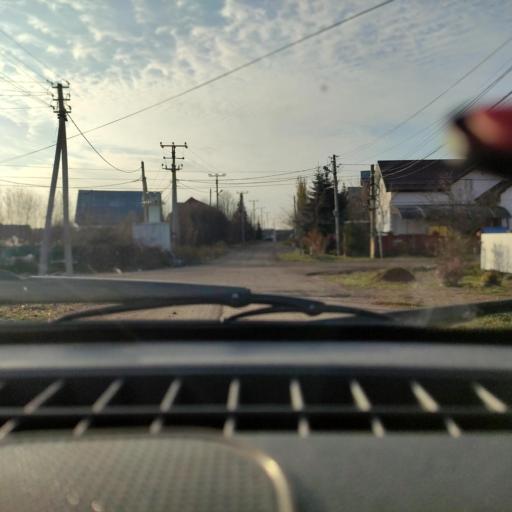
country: RU
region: Bashkortostan
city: Ufa
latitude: 54.6089
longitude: 55.9306
